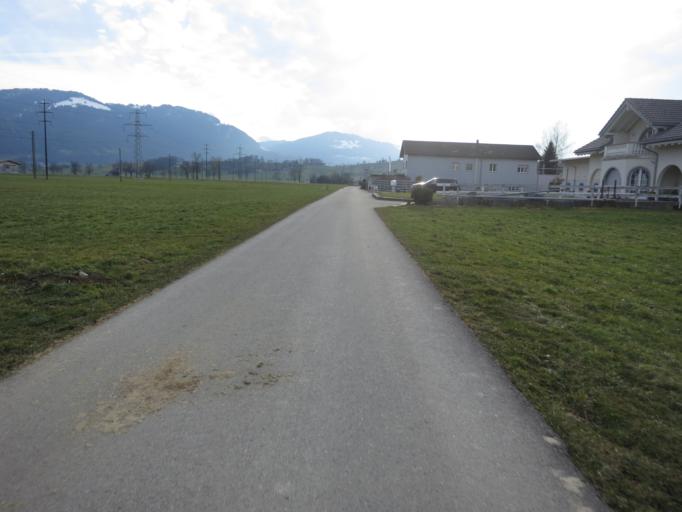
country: CH
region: Schwyz
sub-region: Bezirk March
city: Tuggen
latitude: 47.2032
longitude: 8.9528
